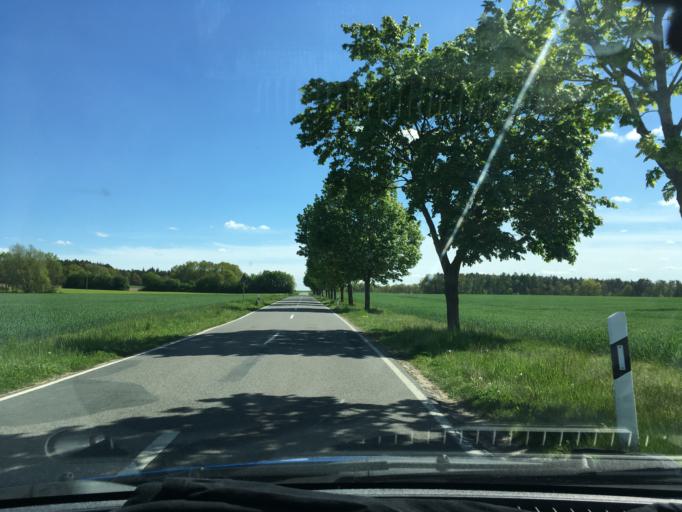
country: DE
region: Lower Saxony
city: Zernien
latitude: 53.0458
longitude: 10.8769
